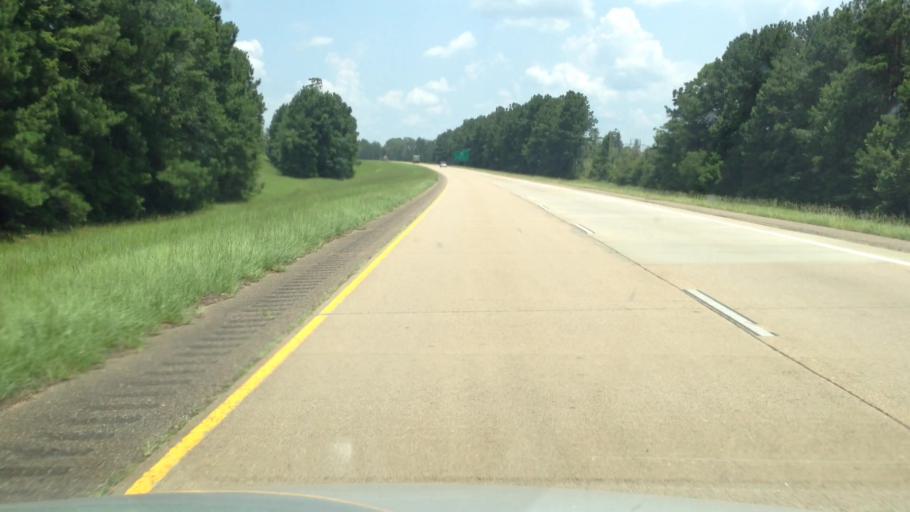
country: US
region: Louisiana
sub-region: Rapides Parish
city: Lecompte
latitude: 31.0337
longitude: -92.4117
